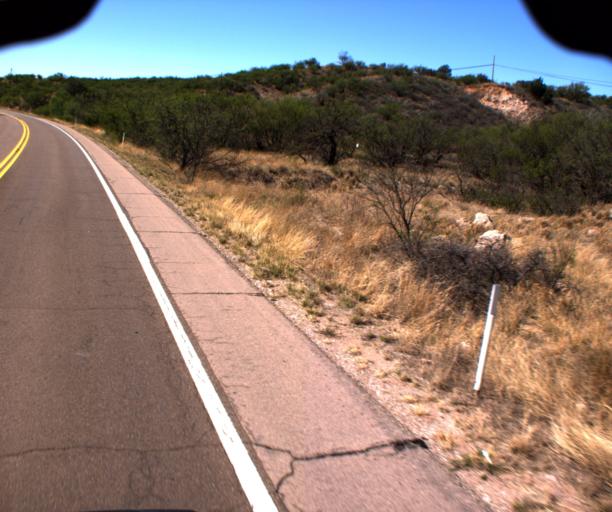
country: US
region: Arizona
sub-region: Santa Cruz County
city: Rio Rico
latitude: 31.6494
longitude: -110.7156
